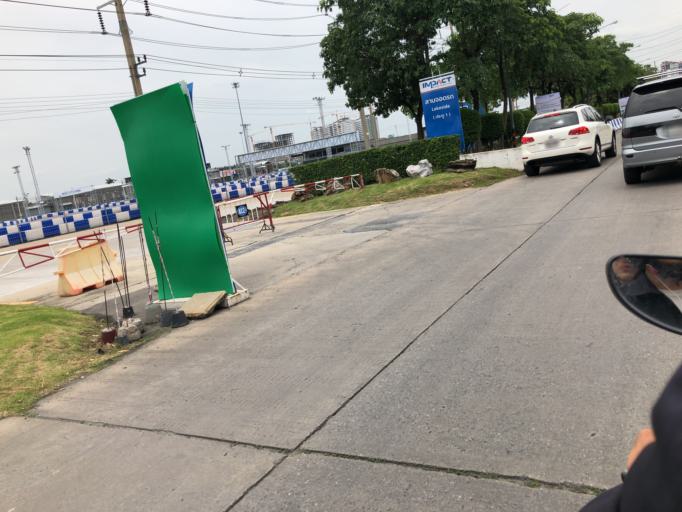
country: TH
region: Nonthaburi
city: Pak Kret
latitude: 13.9178
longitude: 100.5417
